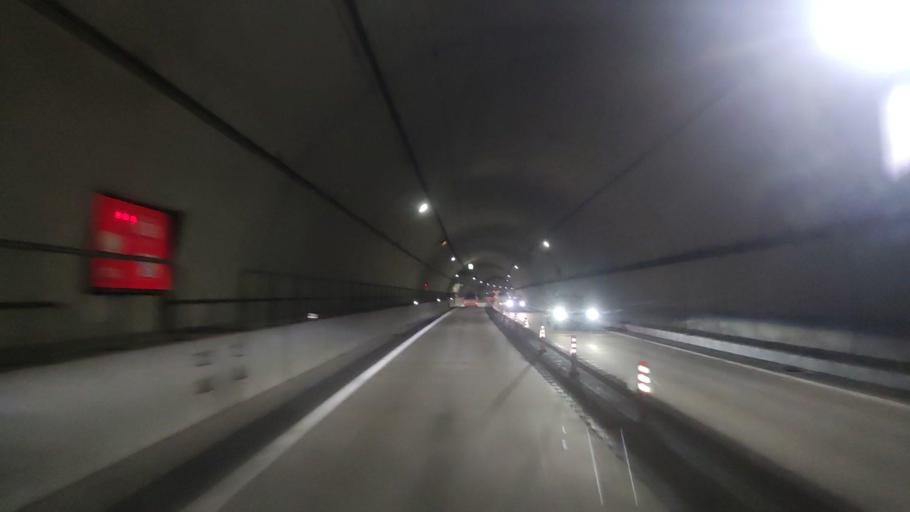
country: JP
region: Wakayama
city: Tanabe
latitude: 33.5884
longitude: 135.4430
